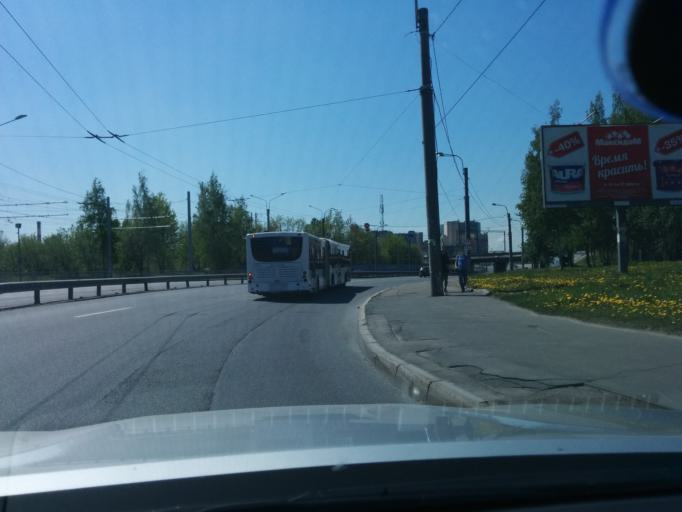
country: RU
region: St.-Petersburg
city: Krasnogvargeisky
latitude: 59.9382
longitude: 30.4509
